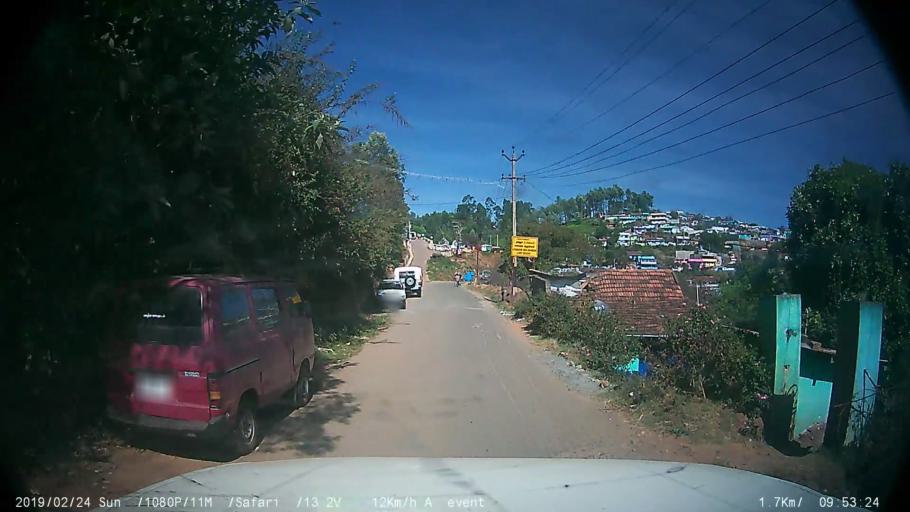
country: IN
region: Tamil Nadu
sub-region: Nilgiri
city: Wellington
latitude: 11.3547
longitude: 76.7729
